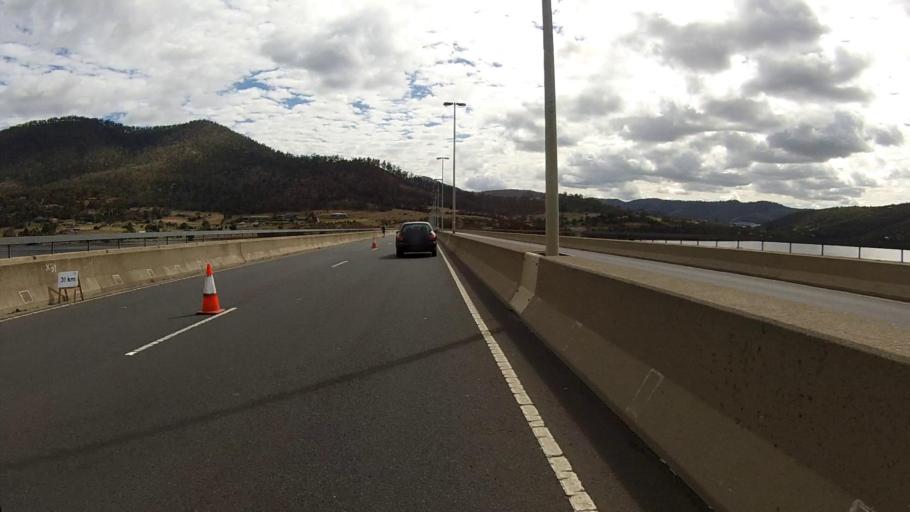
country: AU
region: Tasmania
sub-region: Glenorchy
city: Goodwood
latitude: -42.8192
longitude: 147.3053
